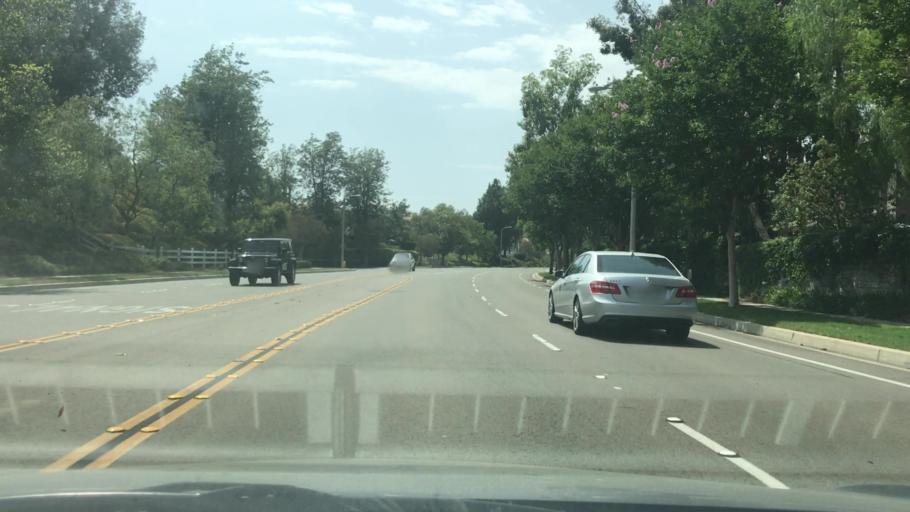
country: US
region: California
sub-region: San Bernardino County
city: Los Serranos
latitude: 33.9304
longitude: -117.6646
